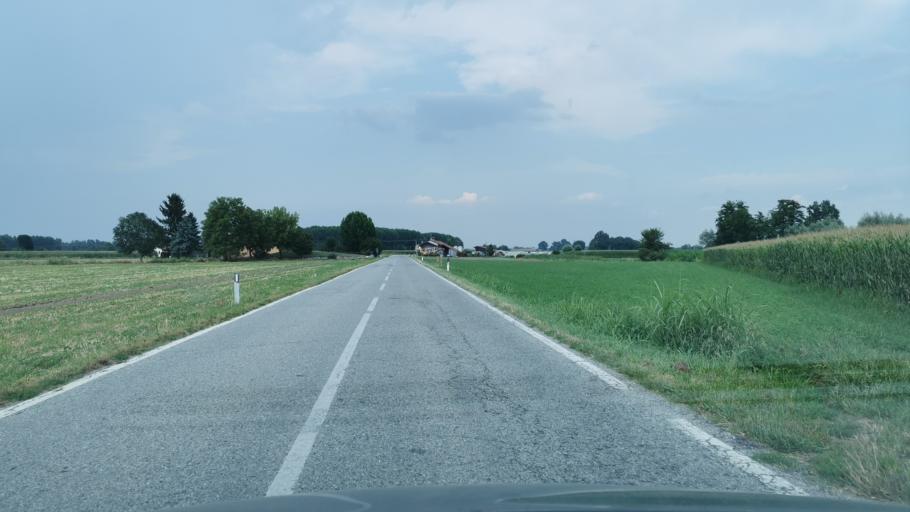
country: IT
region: Piedmont
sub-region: Provincia di Cuneo
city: Vottignasco
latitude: 44.5698
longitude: 7.5911
